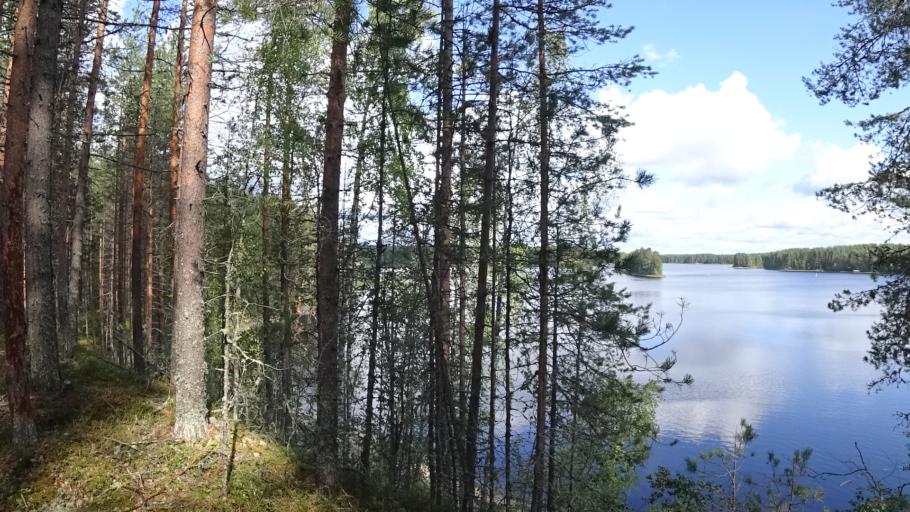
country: FI
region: North Karelia
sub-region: Joensuu
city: Ilomantsi
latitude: 62.6051
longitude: 31.1900
